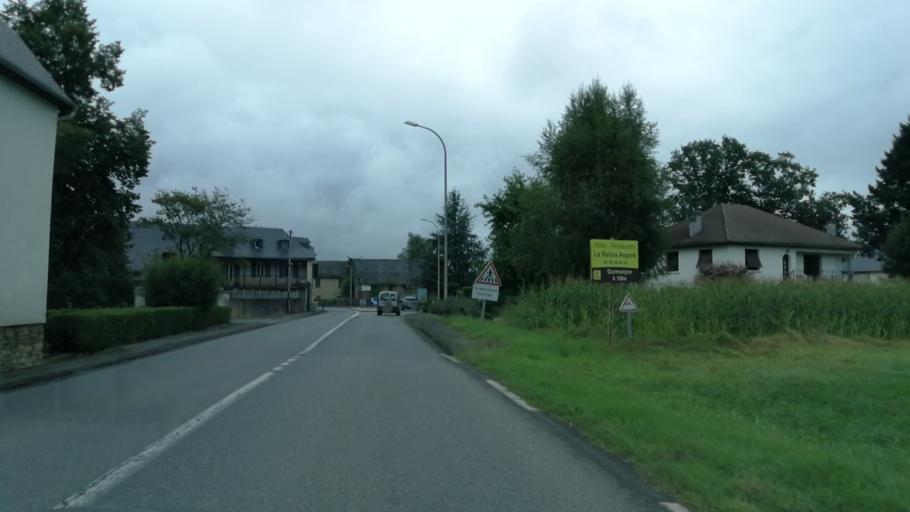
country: FR
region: Aquitaine
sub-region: Departement des Pyrenees-Atlantiques
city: Oloron-Sainte-Marie
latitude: 43.1534
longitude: -0.5971
